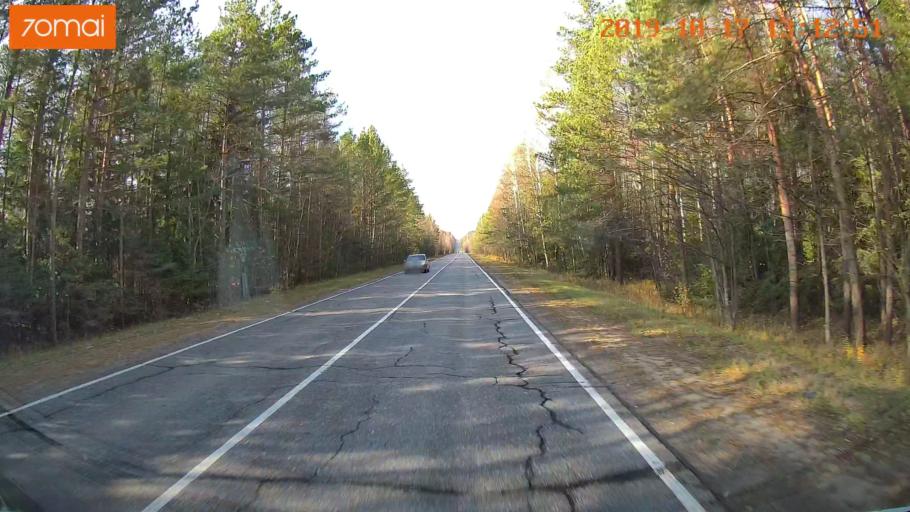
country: RU
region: Rjazan
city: Gus'-Zheleznyy
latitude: 55.0400
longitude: 41.2038
